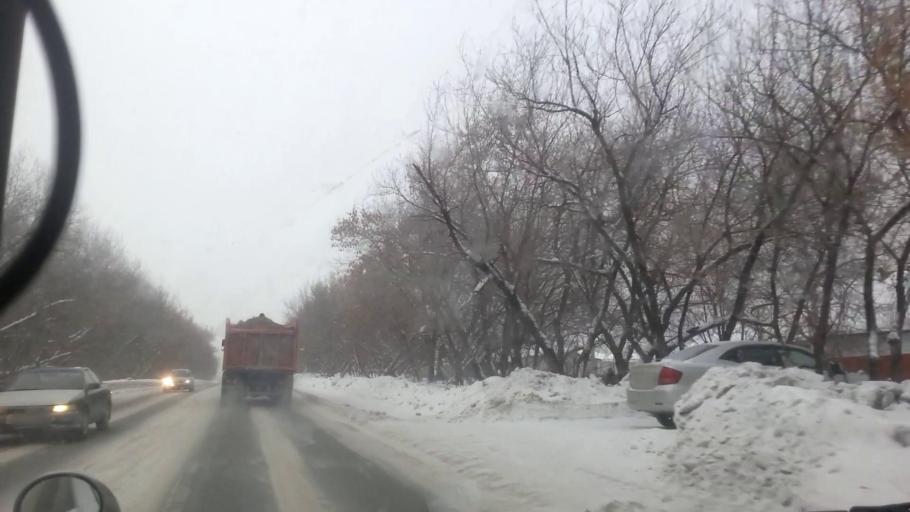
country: RU
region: Altai Krai
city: Vlasikha
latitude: 53.3002
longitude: 83.5947
